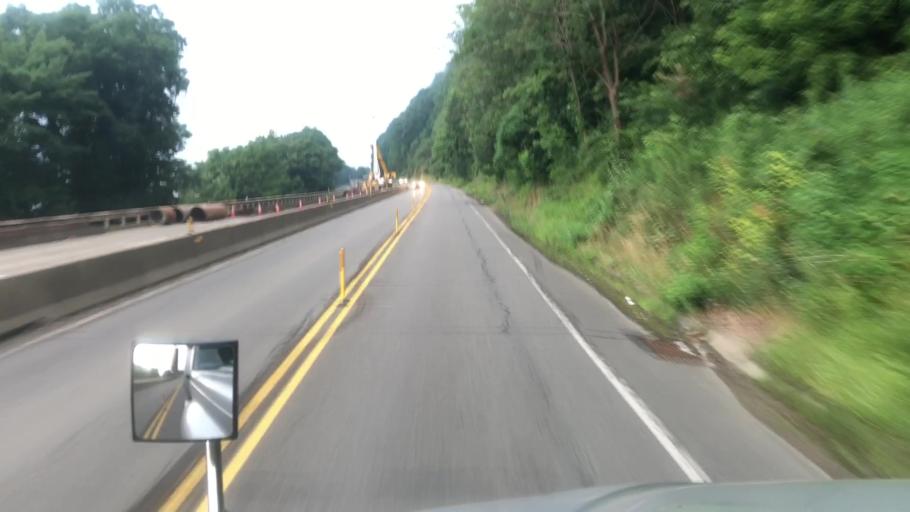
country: US
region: Pennsylvania
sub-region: Venango County
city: Woodland Heights
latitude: 41.4192
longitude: -79.7313
